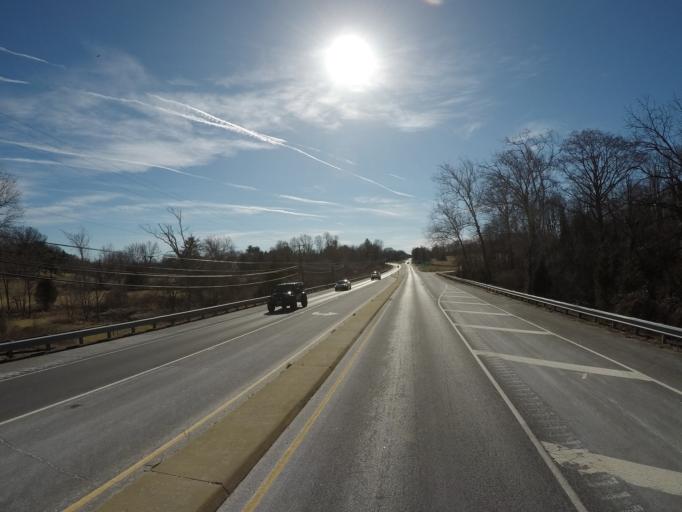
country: US
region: Virginia
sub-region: Loudoun County
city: Leesburg
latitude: 39.1429
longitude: -77.5453
